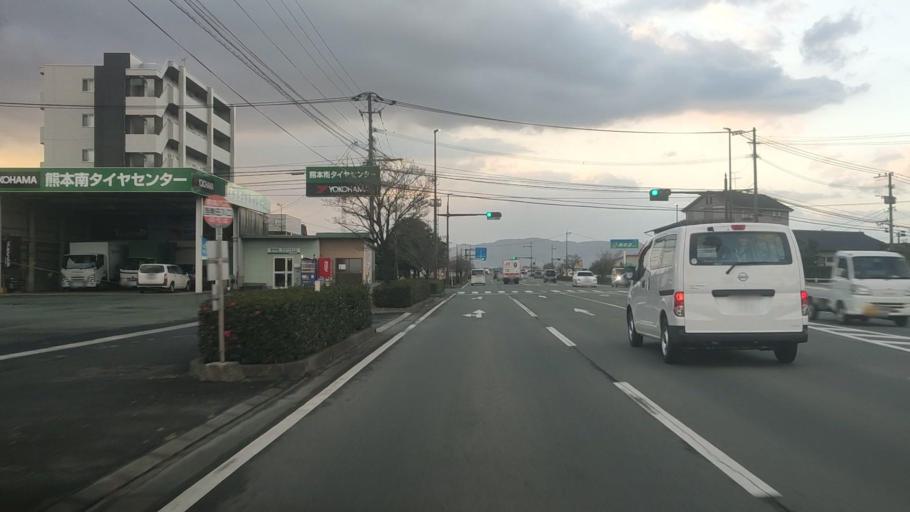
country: JP
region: Kumamoto
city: Kumamoto
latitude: 32.7598
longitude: 130.7058
